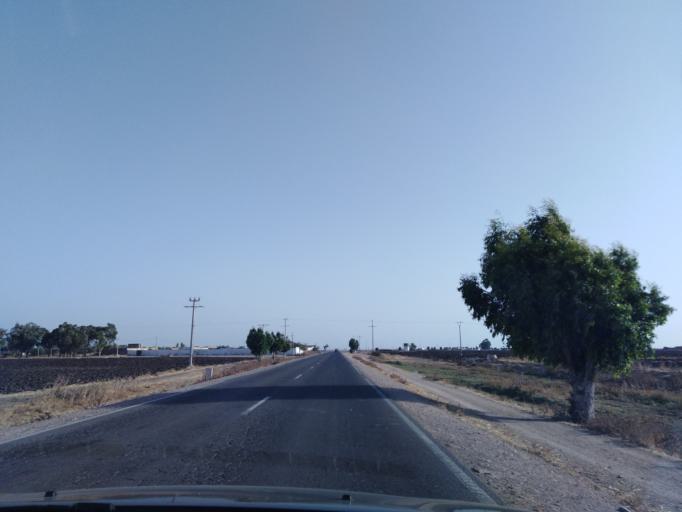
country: MA
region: Doukkala-Abda
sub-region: Safi
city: Youssoufia
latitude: 32.4738
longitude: -8.7720
